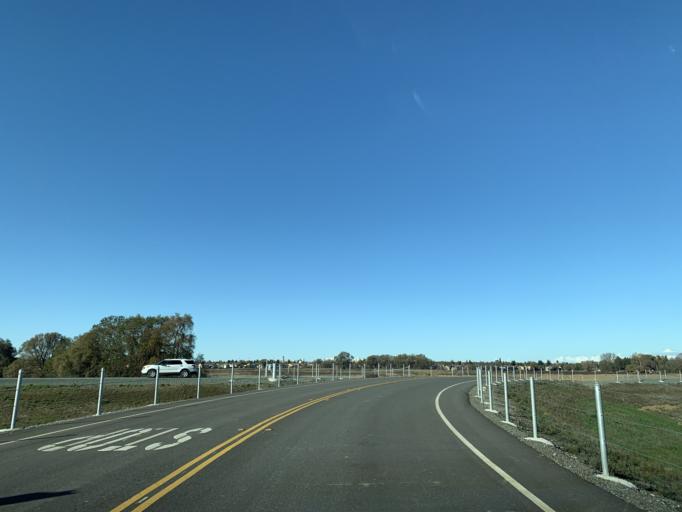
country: US
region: California
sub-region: Yolo County
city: West Sacramento
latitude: 38.5334
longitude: -121.5306
